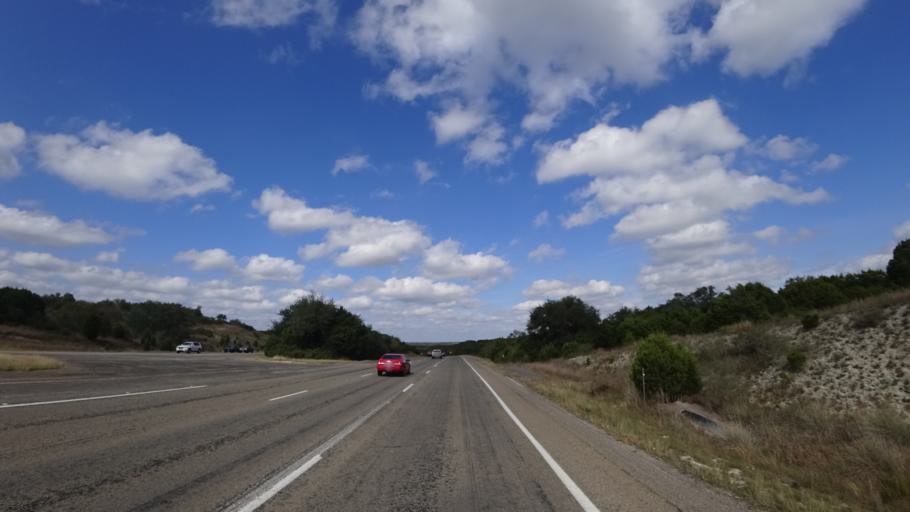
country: US
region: Texas
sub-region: Travis County
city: Barton Creek
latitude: 30.2750
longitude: -97.8978
